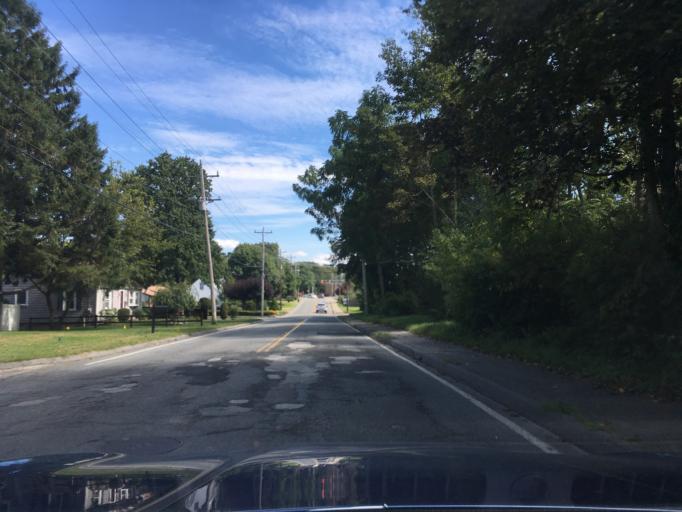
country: US
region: Rhode Island
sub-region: Kent County
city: East Greenwich
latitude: 41.6443
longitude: -71.4682
